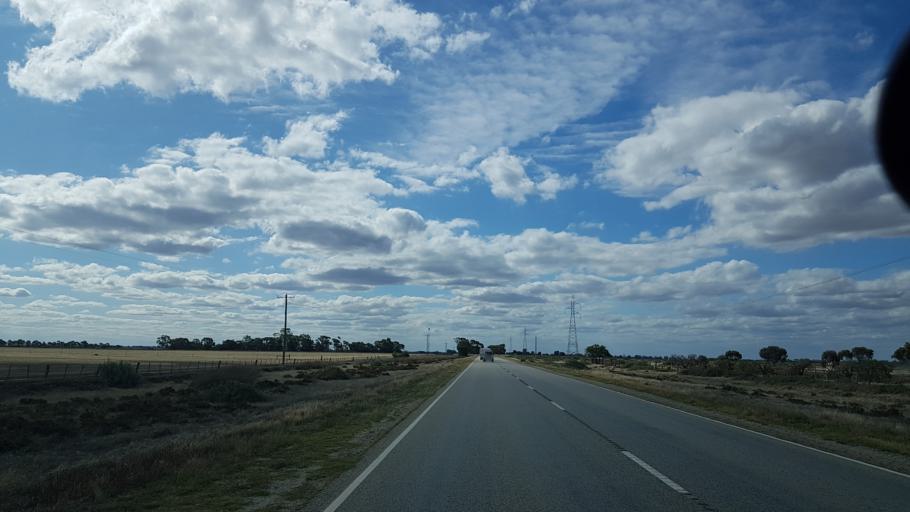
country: AU
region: Victoria
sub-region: Swan Hill
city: Swan Hill
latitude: -35.8858
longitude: 143.9414
